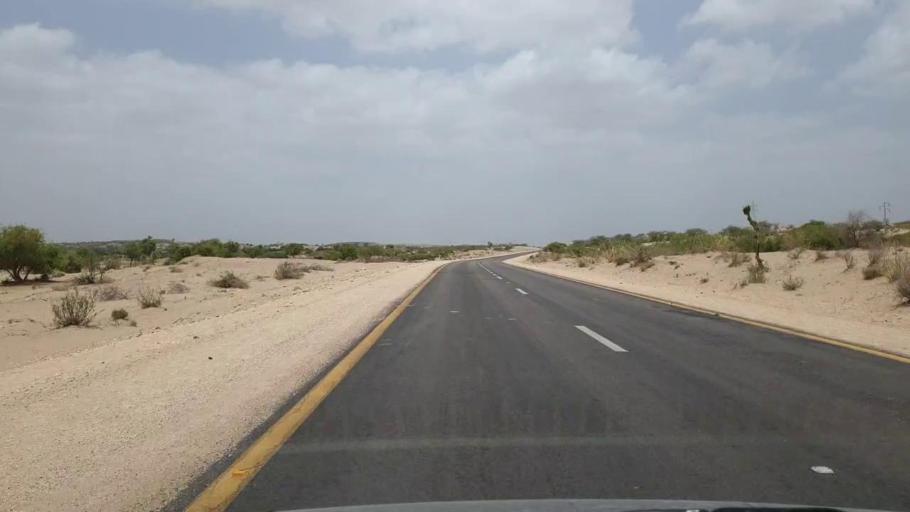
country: PK
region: Sindh
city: Naukot
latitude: 24.8446
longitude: 69.5397
